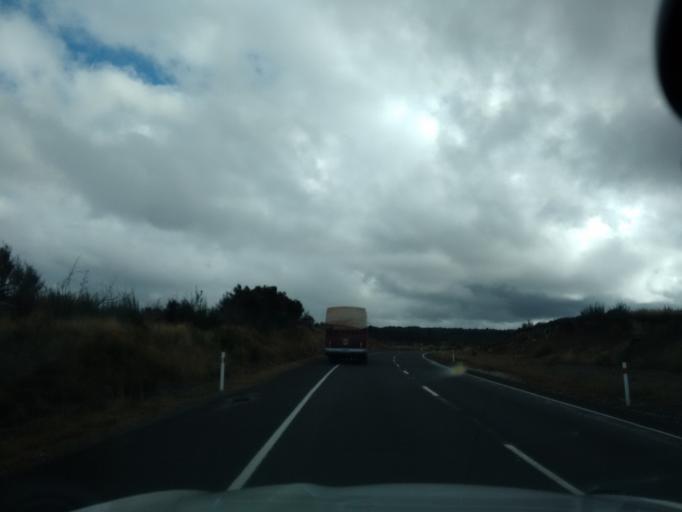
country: NZ
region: Waikato
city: Turangi
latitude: -39.0652
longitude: 175.5742
